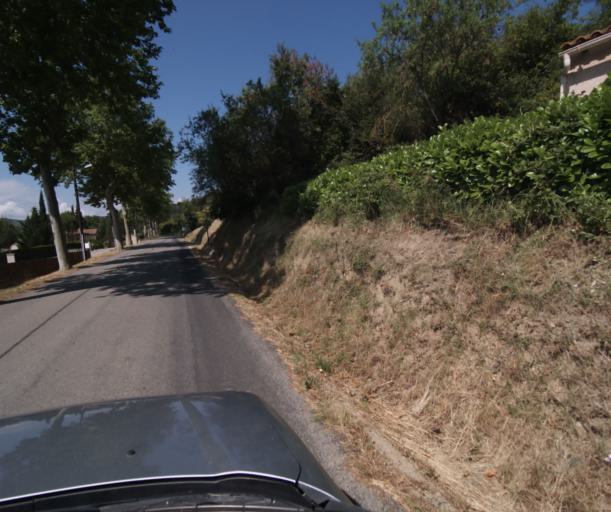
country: FR
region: Languedoc-Roussillon
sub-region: Departement de l'Aude
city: Limoux
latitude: 43.0435
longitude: 2.2195
